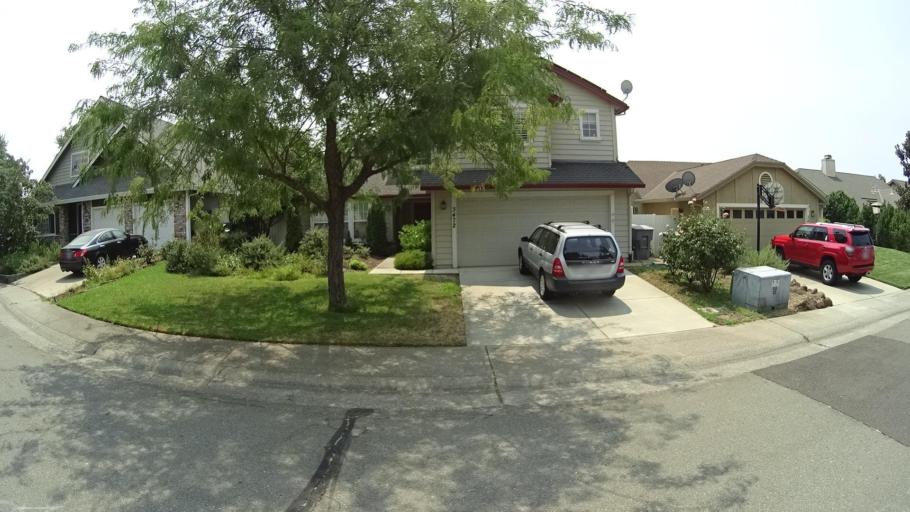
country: US
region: California
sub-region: Placer County
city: Rocklin
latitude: 38.8005
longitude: -121.2580
